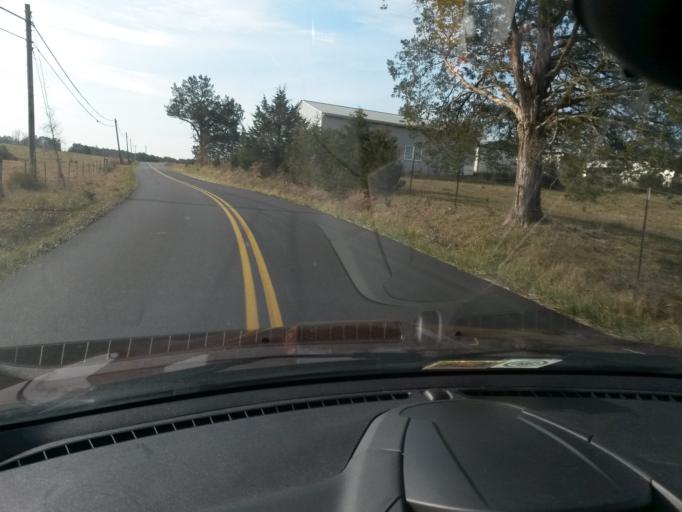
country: US
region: Virginia
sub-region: Botetourt County
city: Fincastle
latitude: 37.5361
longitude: -79.8788
